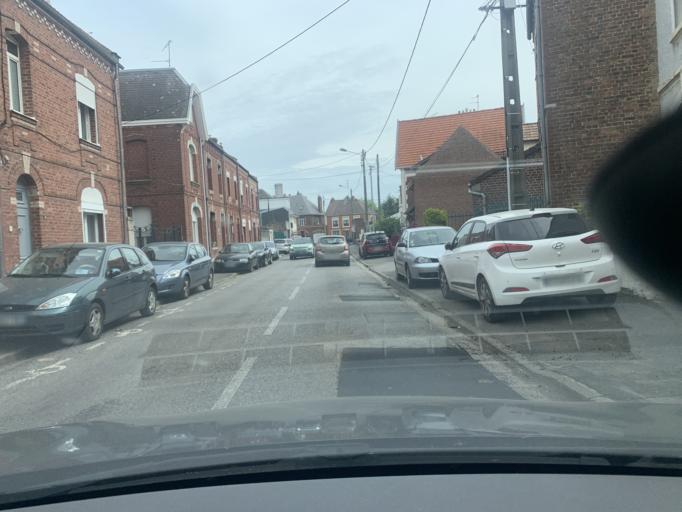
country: FR
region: Nord-Pas-de-Calais
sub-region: Departement du Nord
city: Cambrai
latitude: 50.1650
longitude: 3.2378
